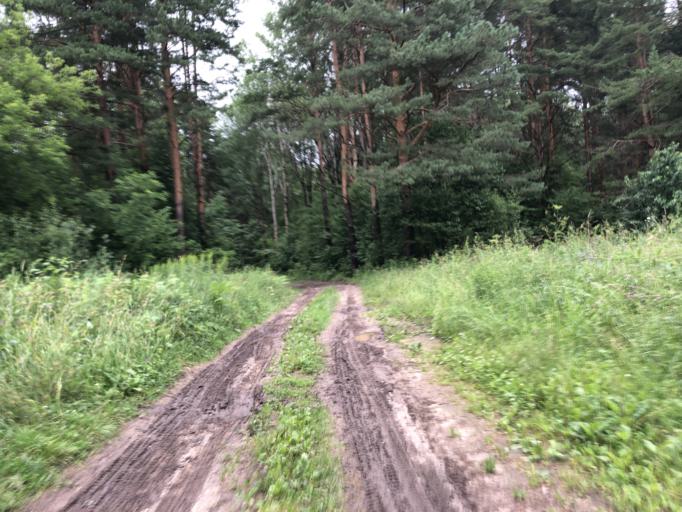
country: RU
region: Tverskaya
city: Rzhev
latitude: 56.2465
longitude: 34.3706
